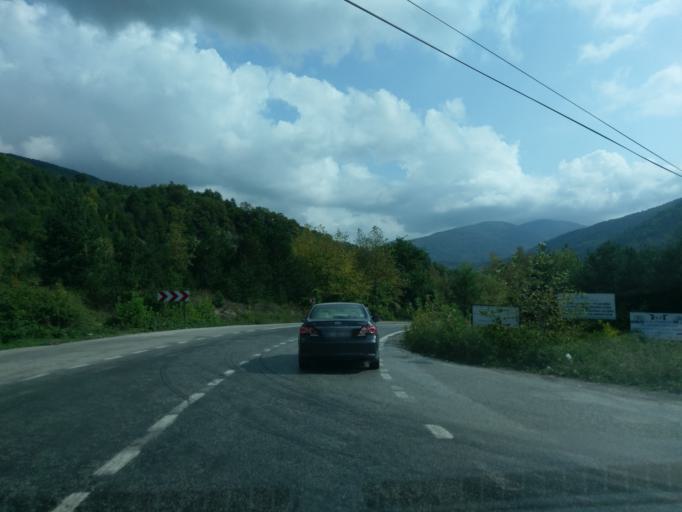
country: TR
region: Sinop
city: Yenikonak
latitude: 41.8772
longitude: 34.5489
